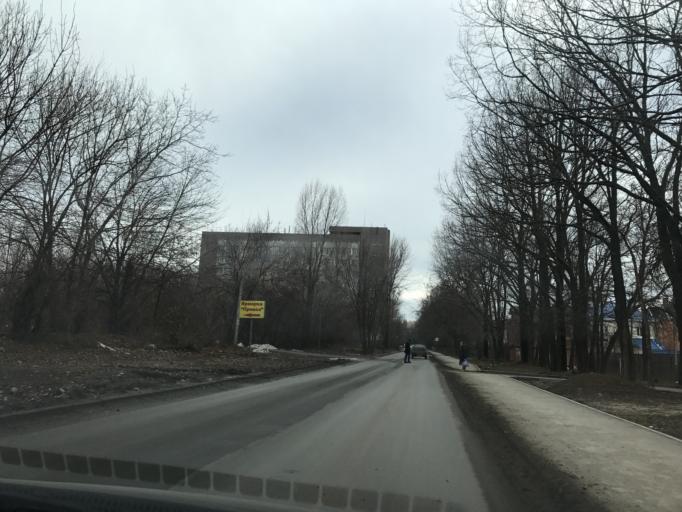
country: RU
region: Rostov
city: Rostov-na-Donu
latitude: 47.2209
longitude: 39.6267
